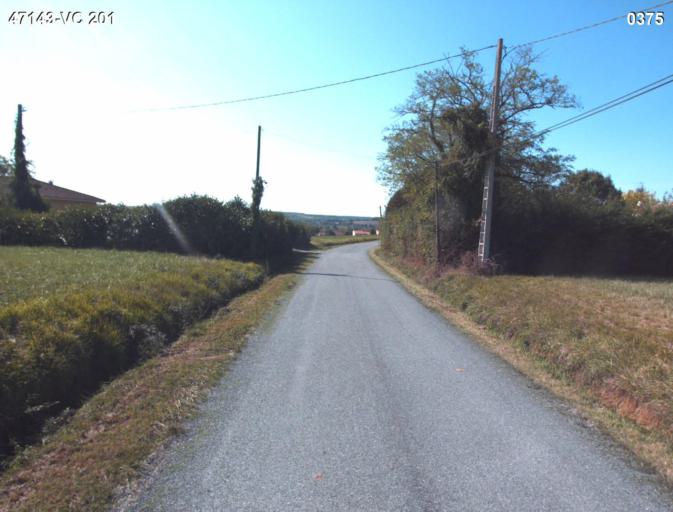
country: FR
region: Aquitaine
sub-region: Departement du Lot-et-Garonne
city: Lavardac
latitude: 44.1826
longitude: 0.3129
